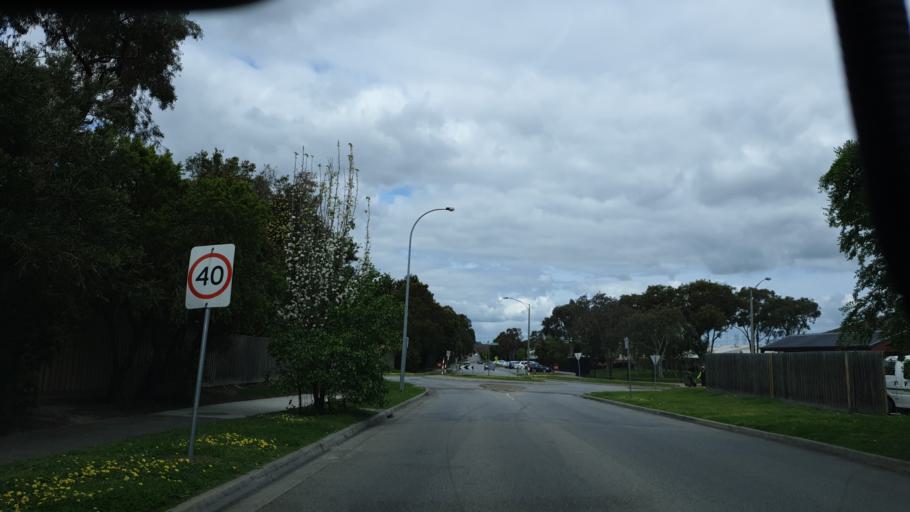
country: AU
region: Victoria
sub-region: Casey
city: Cranbourne North
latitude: -38.0783
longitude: 145.2842
